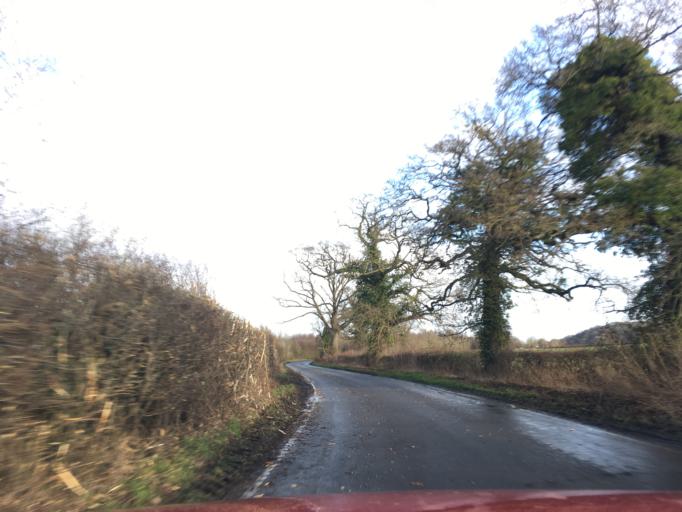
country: GB
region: England
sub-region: Warwickshire
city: Alcester
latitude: 52.2252
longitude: -1.8179
